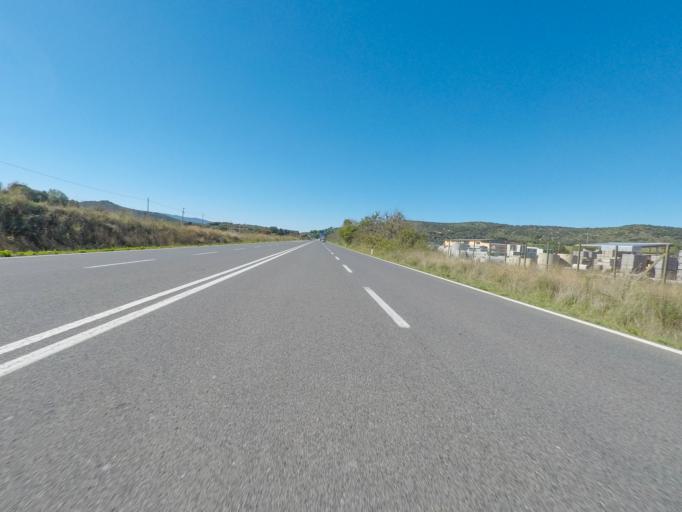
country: IT
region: Tuscany
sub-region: Provincia di Grosseto
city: Orbetello Scalo
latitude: 42.4170
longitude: 11.3100
